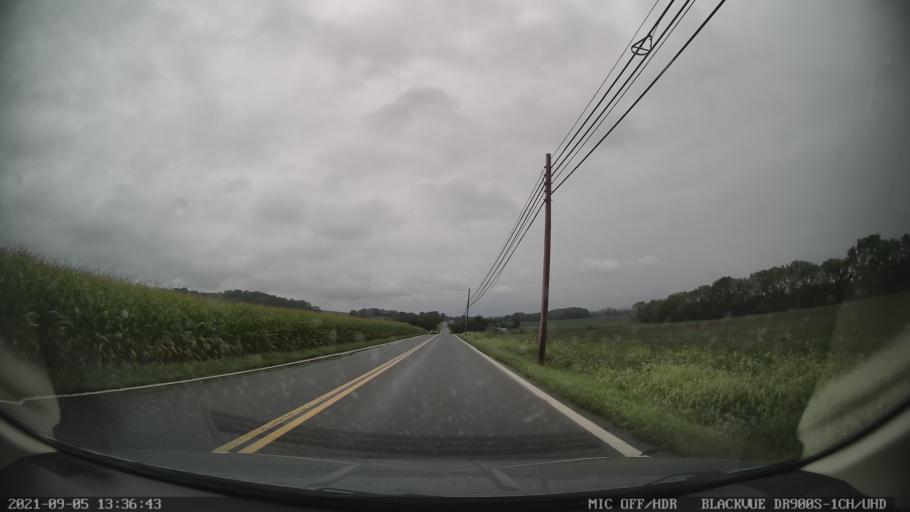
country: US
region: Pennsylvania
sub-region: Lehigh County
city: Breinigsville
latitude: 40.5794
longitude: -75.6513
